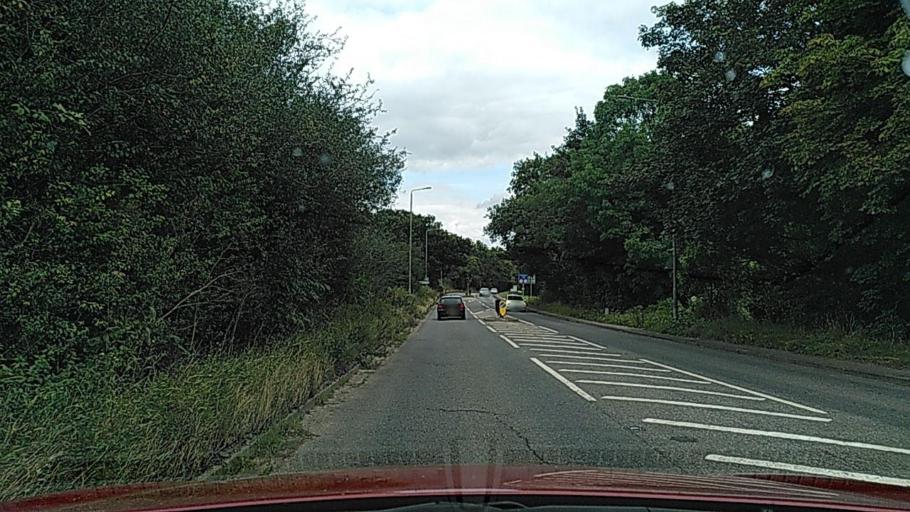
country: GB
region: England
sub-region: Royal Borough of Windsor and Maidenhead
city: Hurley
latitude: 51.5117
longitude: -0.8107
